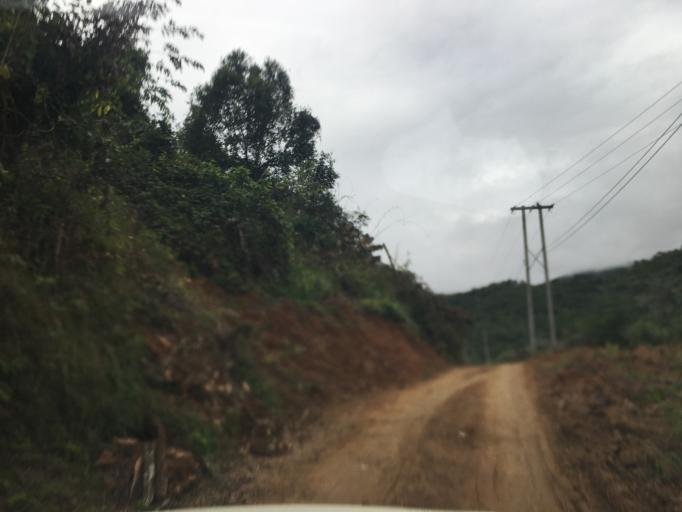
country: LA
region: Houaphan
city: Viengthong
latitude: 19.9398
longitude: 103.2869
